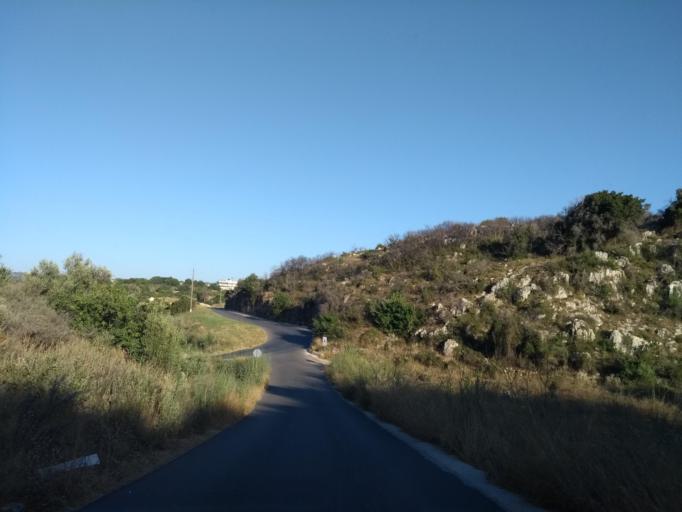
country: GR
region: Crete
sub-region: Nomos Chanias
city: Kalivai
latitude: 35.4296
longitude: 24.1776
